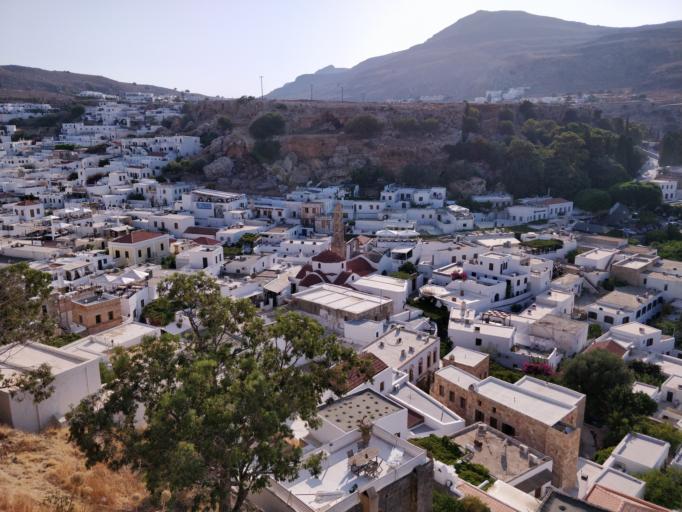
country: GR
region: South Aegean
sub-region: Nomos Dodekanisou
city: Lardos
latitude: 36.0921
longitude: 28.0870
